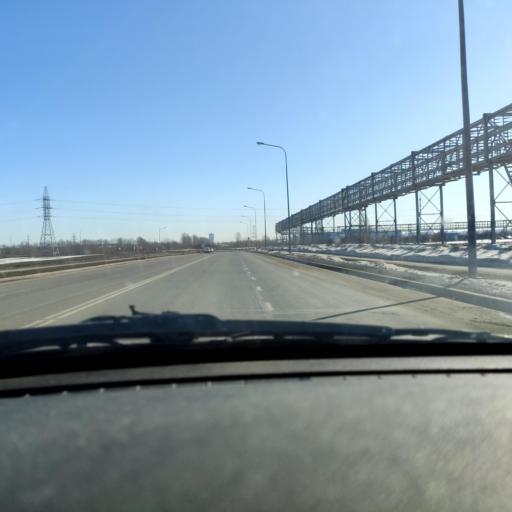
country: RU
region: Samara
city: Podstepki
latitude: 53.5595
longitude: 49.2012
